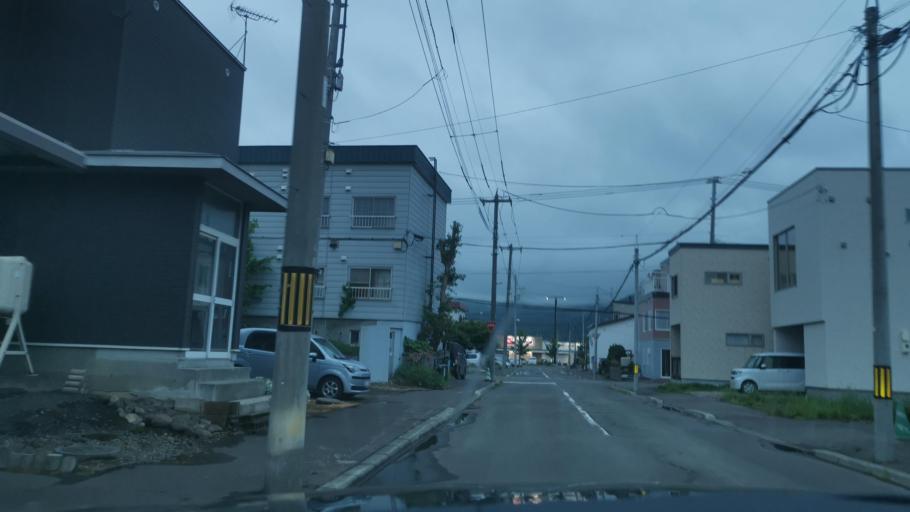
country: JP
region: Hokkaido
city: Sapporo
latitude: 43.1080
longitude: 141.2745
